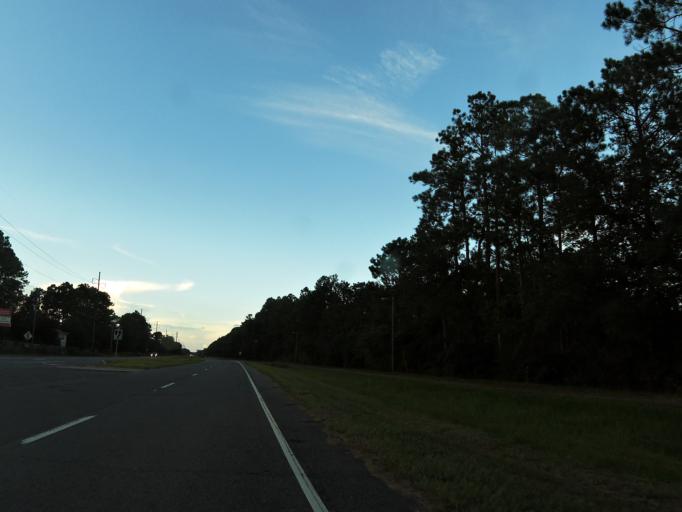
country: US
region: Georgia
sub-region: Camden County
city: St Marys
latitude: 30.7696
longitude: -81.5764
